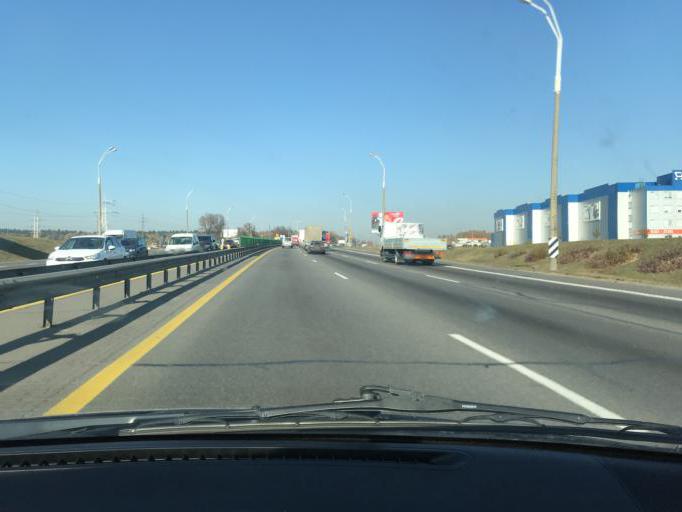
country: BY
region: Minsk
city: Novoye Medvezhino
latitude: 53.9001
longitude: 27.4079
